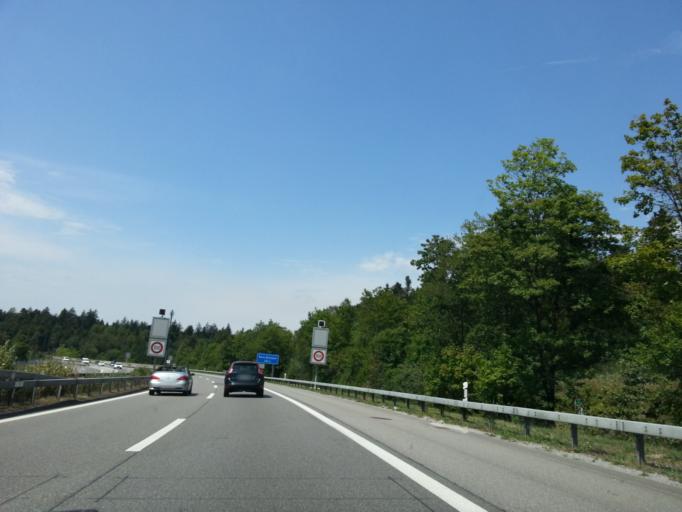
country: CH
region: Bern
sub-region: Bern-Mittelland District
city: Koniz
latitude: 46.9543
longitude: 7.3942
